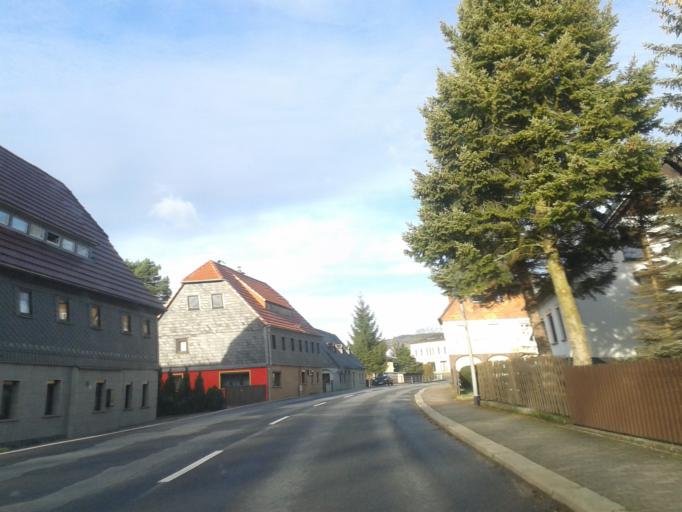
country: DE
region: Saxony
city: Eibau
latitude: 50.9770
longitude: 14.6682
